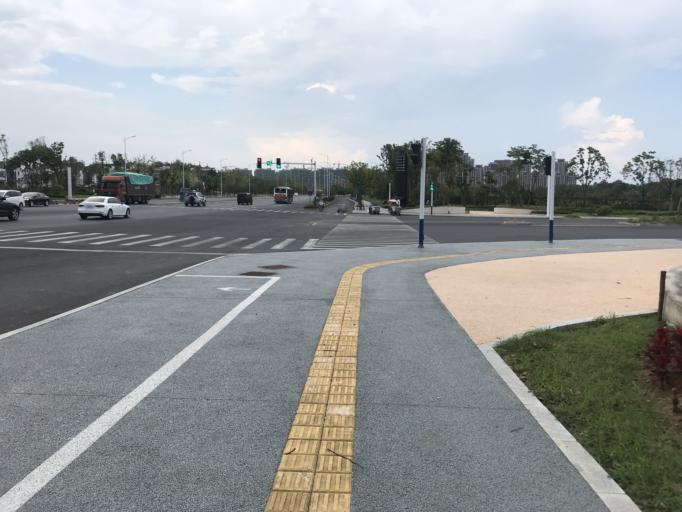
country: CN
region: Anhui Sheng
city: Wan'an
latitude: 29.7997
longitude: 118.2640
